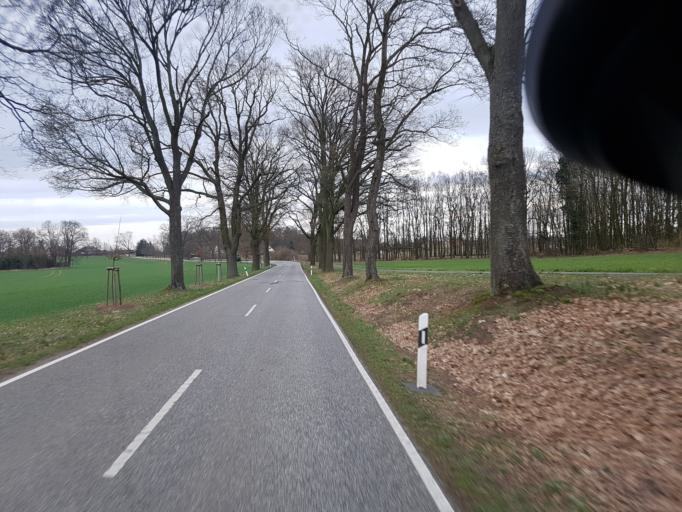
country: DE
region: Brandenburg
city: Mixdorf
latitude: 52.1963
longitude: 14.3364
